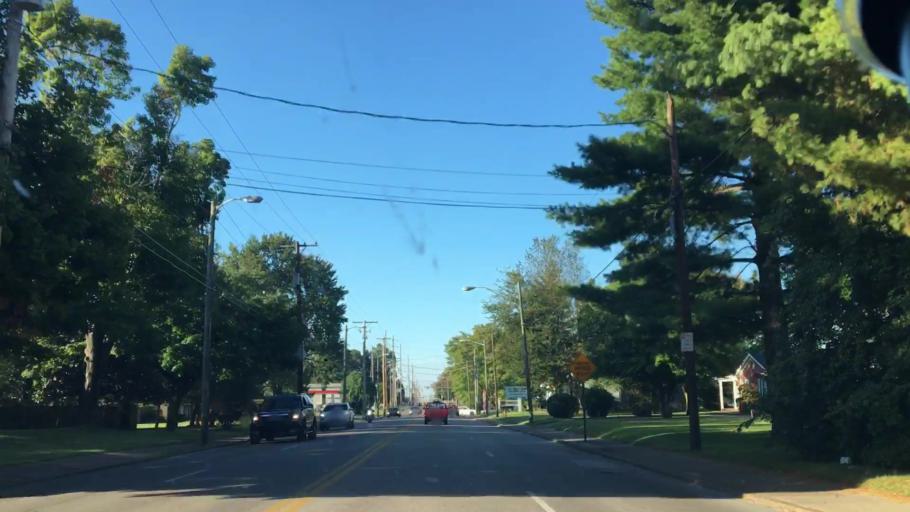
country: US
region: Indiana
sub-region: Vanderburgh County
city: Evansville
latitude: 37.9524
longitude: -87.4929
